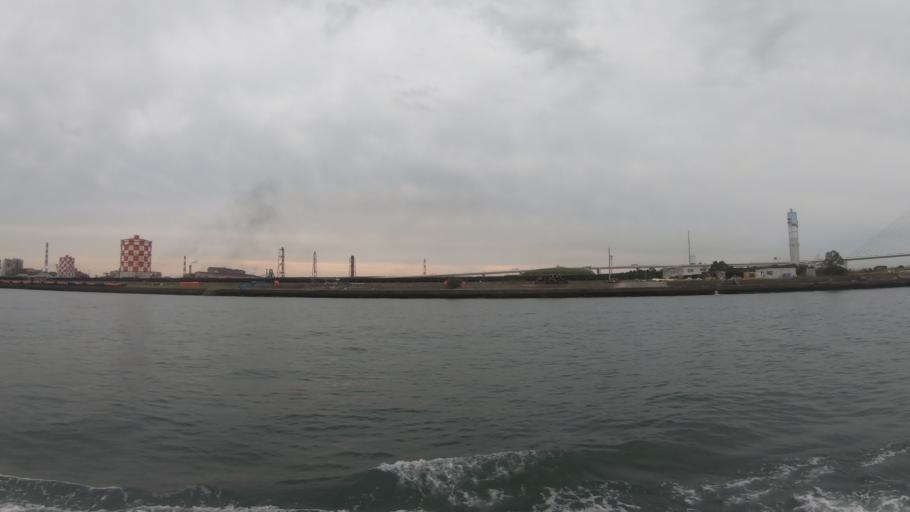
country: JP
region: Kanagawa
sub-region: Kawasaki-shi
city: Kawasaki
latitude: 35.4830
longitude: 139.7053
